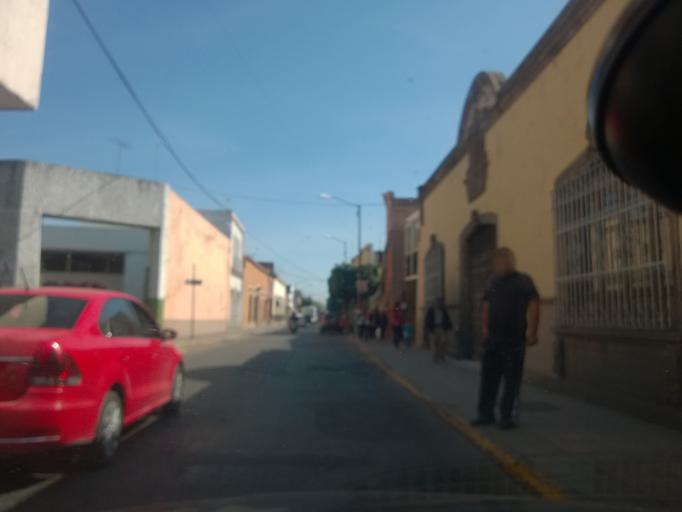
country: MX
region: Guanajuato
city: Leon
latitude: 21.1204
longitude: -101.6802
